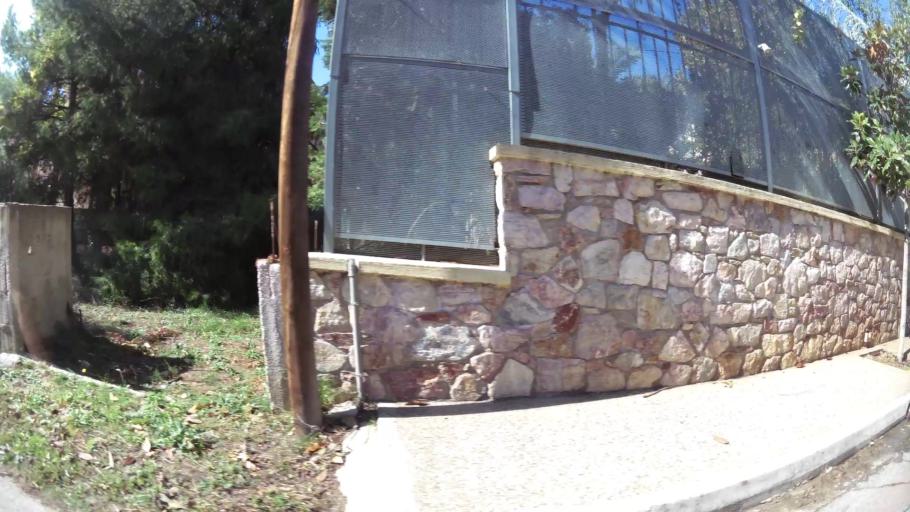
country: GR
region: Attica
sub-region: Nomarchia Anatolikis Attikis
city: Dioni
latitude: 38.0207
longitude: 23.9286
